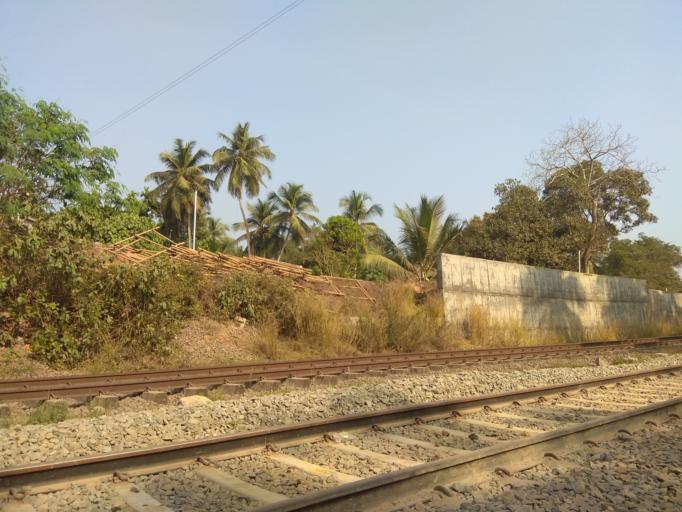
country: IN
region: Karnataka
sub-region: Dakshina Kannada
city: Mangalore
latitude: 12.9156
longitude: 74.8764
